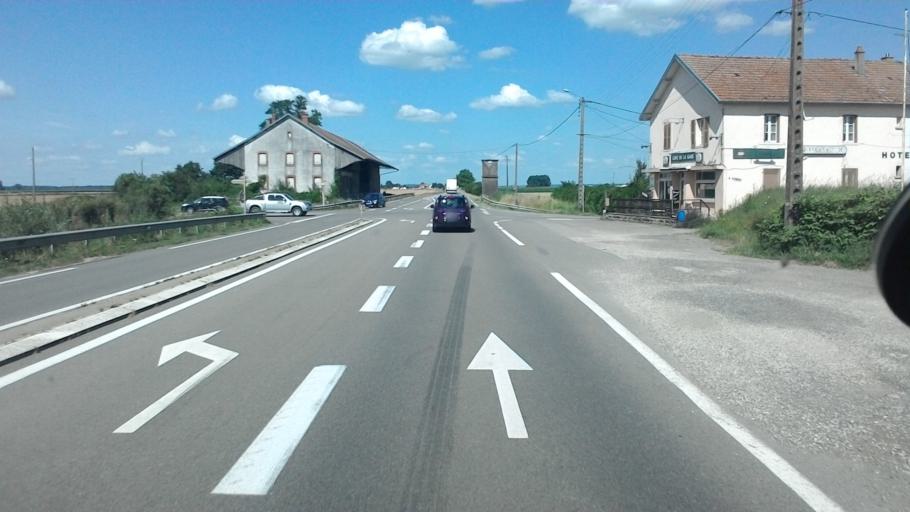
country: FR
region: Franche-Comte
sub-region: Departement du Jura
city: Saint-Aubin
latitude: 46.9956
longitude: 5.3427
